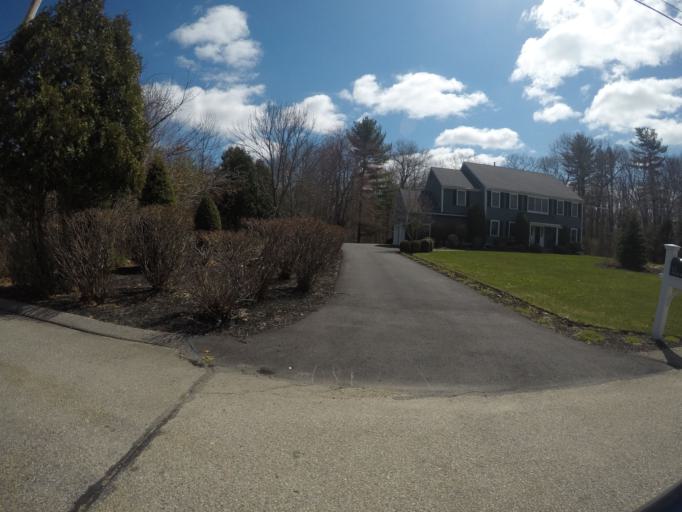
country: US
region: Massachusetts
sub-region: Bristol County
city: Easton
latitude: 42.0693
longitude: -71.1342
